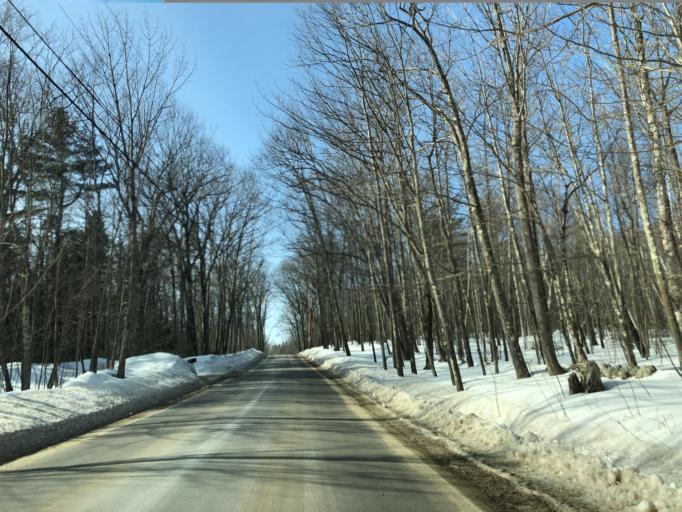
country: US
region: Maine
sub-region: Oxford County
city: Paris
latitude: 44.2663
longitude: -70.4694
